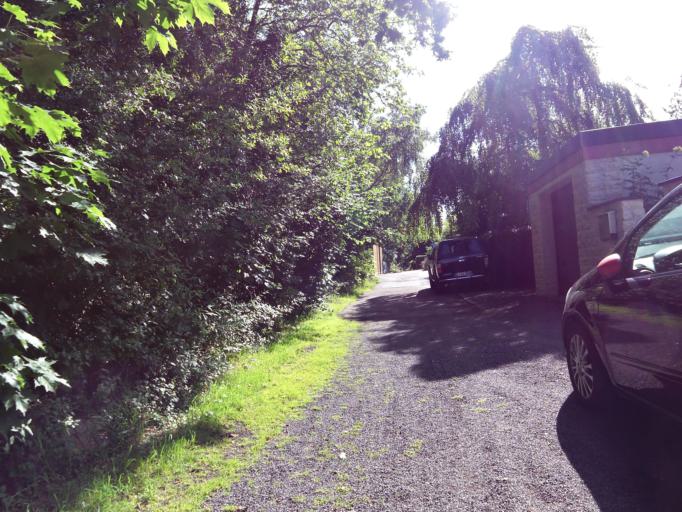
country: DE
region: Saxony
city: Taucha
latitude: 51.3209
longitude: 12.4451
